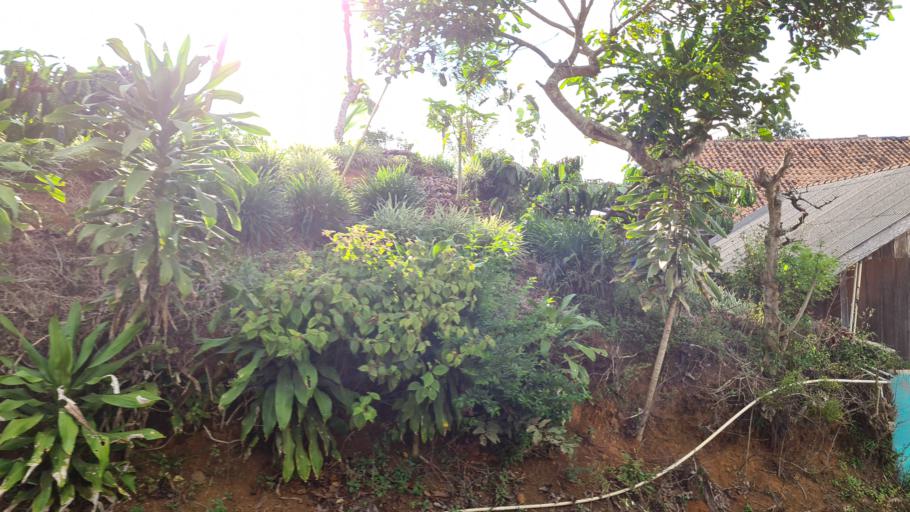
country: ID
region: Lampung
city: Kenali
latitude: -5.0945
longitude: 104.3988
